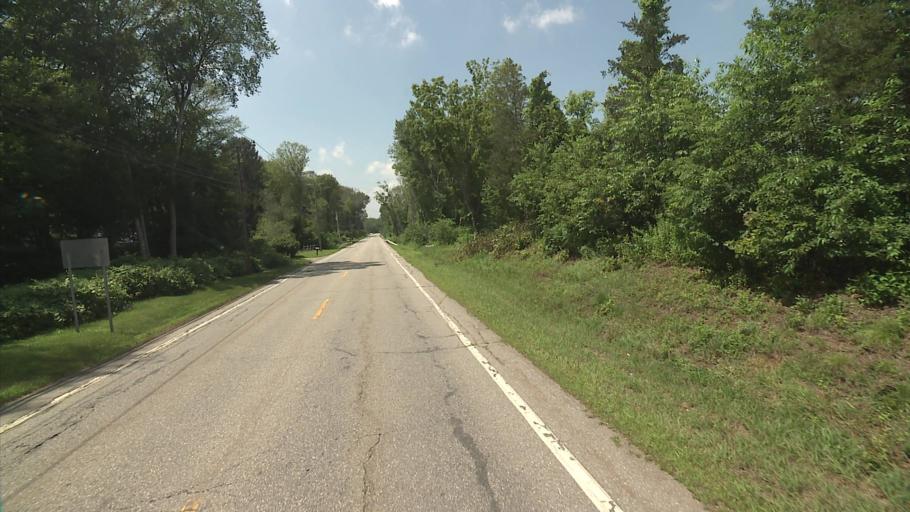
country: US
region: Connecticut
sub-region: New London County
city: Preston City
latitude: 41.5310
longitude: -71.9963
